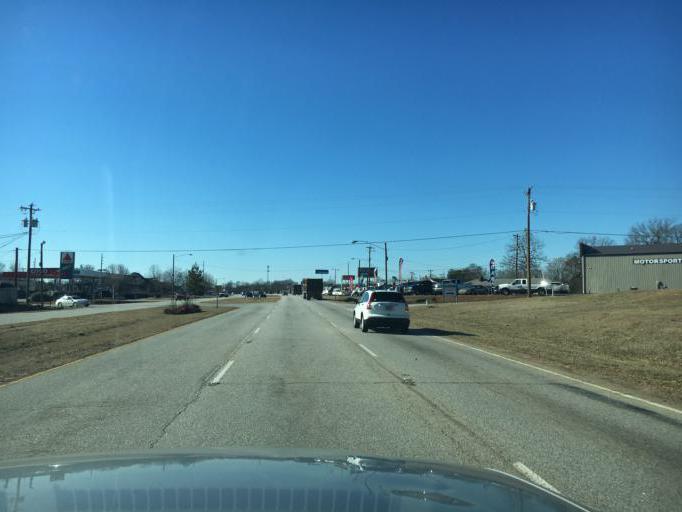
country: US
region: South Carolina
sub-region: Spartanburg County
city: Wellford
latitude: 34.9534
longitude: -82.1111
